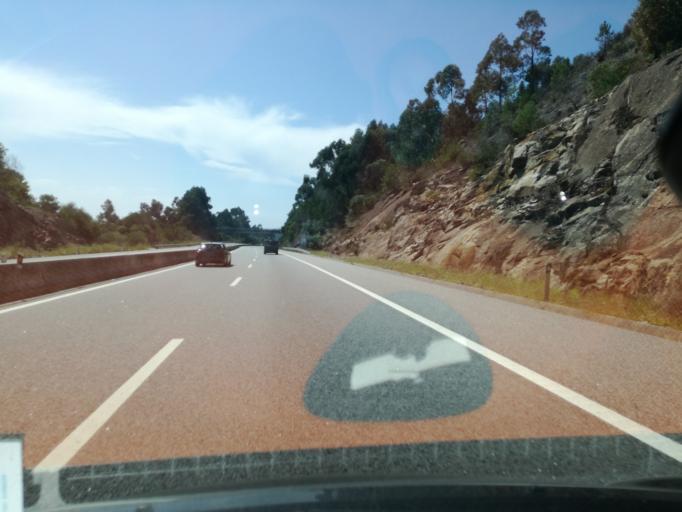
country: PT
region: Viana do Castelo
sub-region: Viana do Castelo
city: Meadela
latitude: 41.7601
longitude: -8.7950
